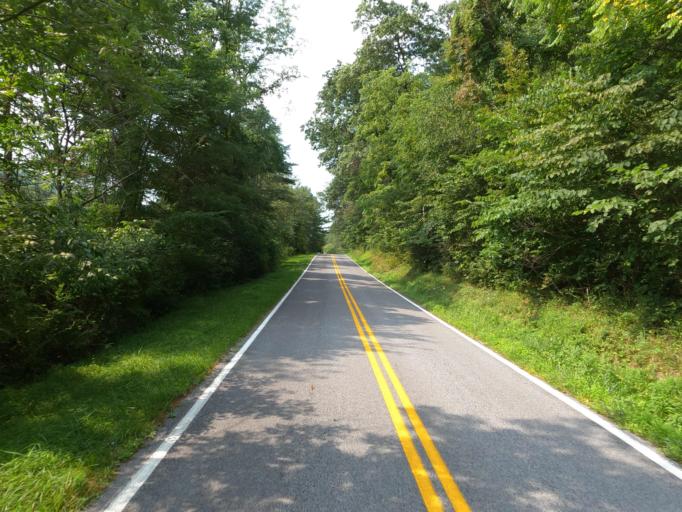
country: US
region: West Virginia
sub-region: Morgan County
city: Berkeley Springs
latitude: 39.6887
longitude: -78.2529
